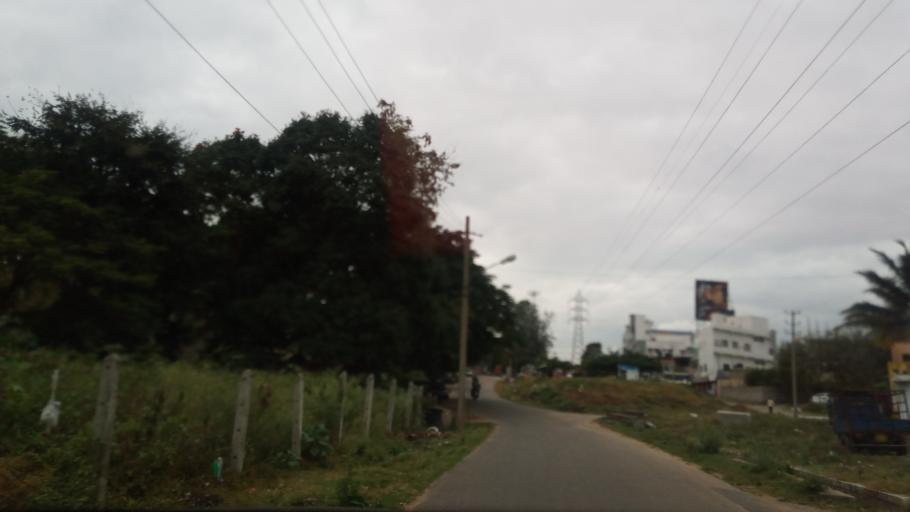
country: IN
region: Karnataka
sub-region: Mysore
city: Mysore
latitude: 12.2944
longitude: 76.6150
